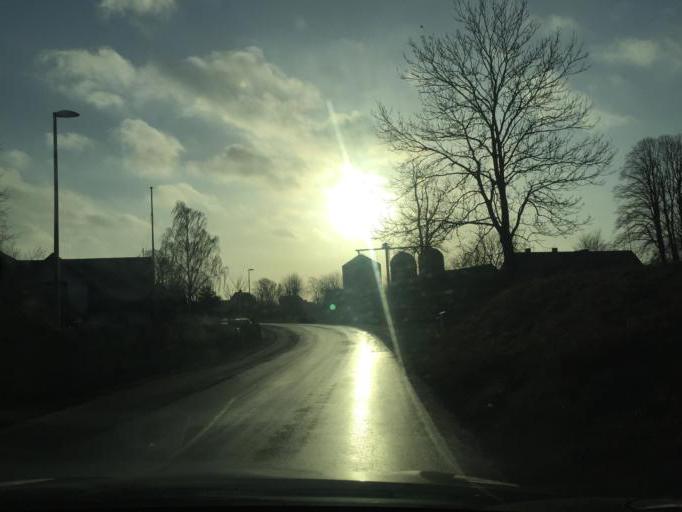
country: DK
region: South Denmark
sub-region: Faaborg-Midtfyn Kommune
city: Ringe
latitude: 55.1915
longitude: 10.3490
